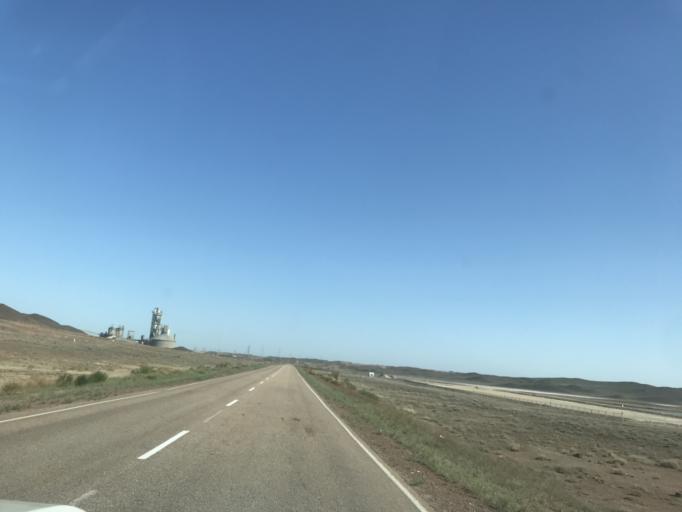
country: KZ
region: Zhambyl
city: Mynaral
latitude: 45.3984
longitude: 73.6403
